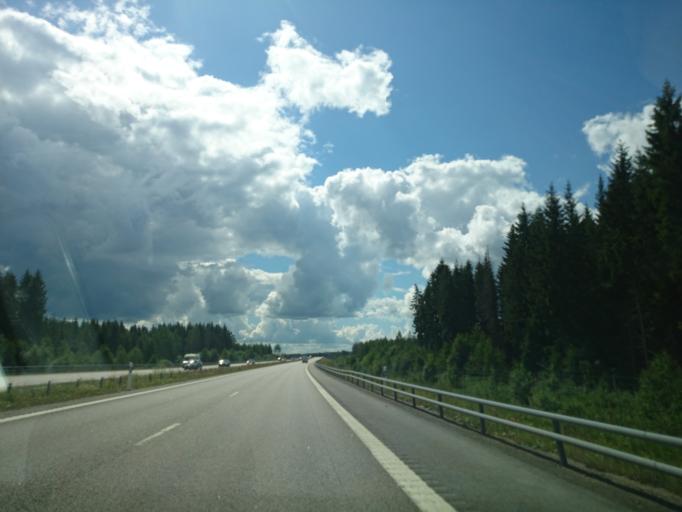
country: SE
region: Uppsala
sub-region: Tierps Kommun
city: Tierp
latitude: 60.3678
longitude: 17.4790
